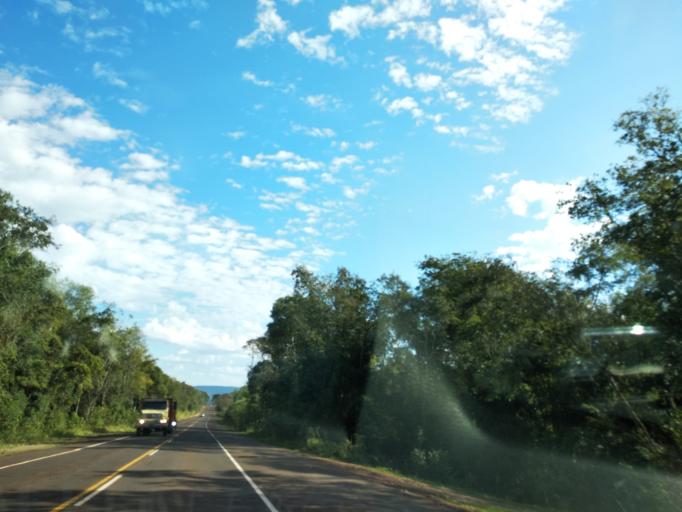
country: AR
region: Misiones
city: Aristobulo del Valle
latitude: -27.0928
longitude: -54.9509
